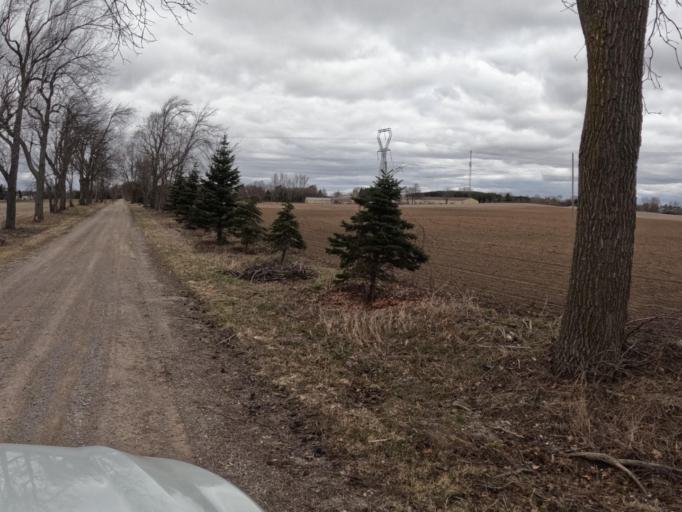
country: CA
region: Ontario
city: Norfolk County
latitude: 42.9639
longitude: -80.3899
